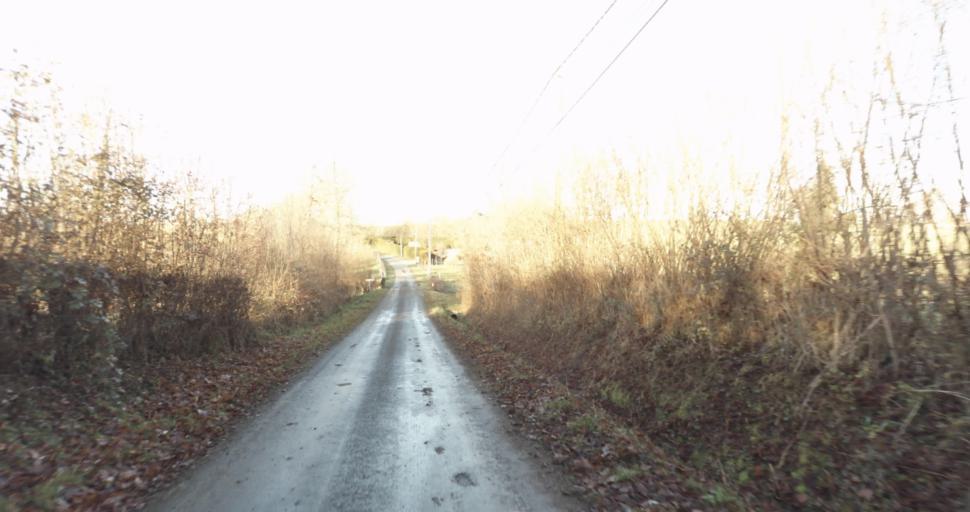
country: FR
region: Limousin
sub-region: Departement de la Haute-Vienne
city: Aixe-sur-Vienne
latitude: 45.7811
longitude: 1.1507
